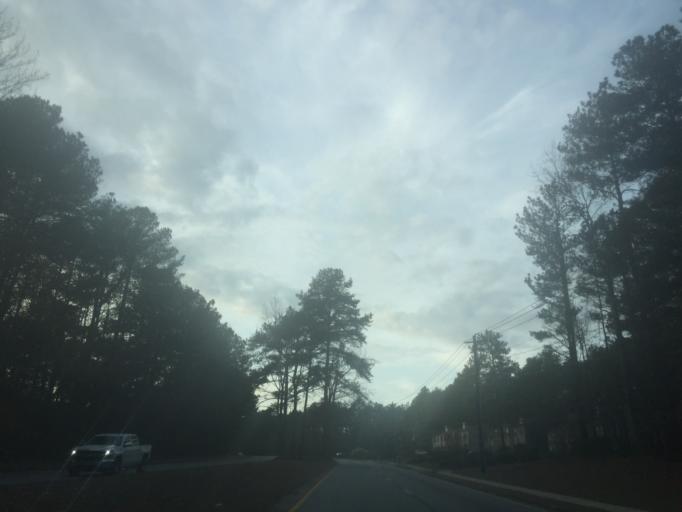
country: US
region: Georgia
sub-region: Clayton County
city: Riverdale
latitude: 33.5952
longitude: -84.4150
